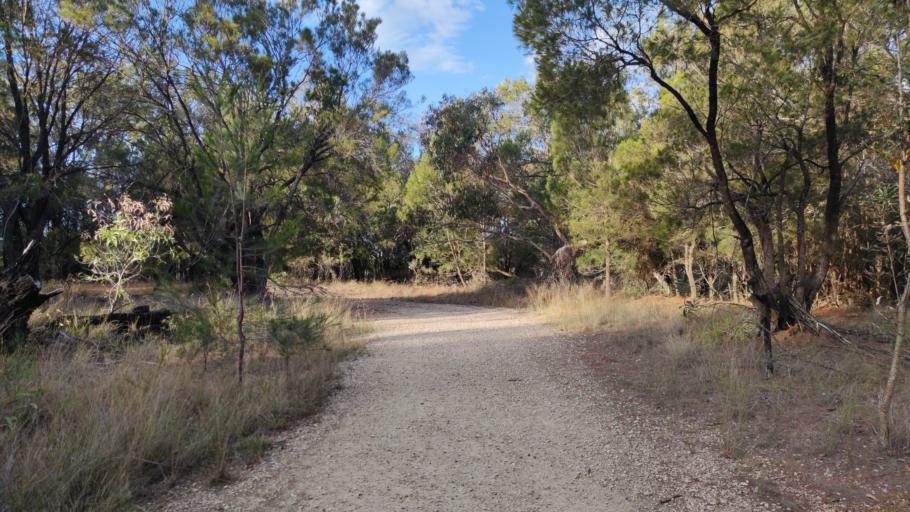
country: AU
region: Queensland
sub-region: Redland
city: Cleveland
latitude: -27.5498
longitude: 153.2437
